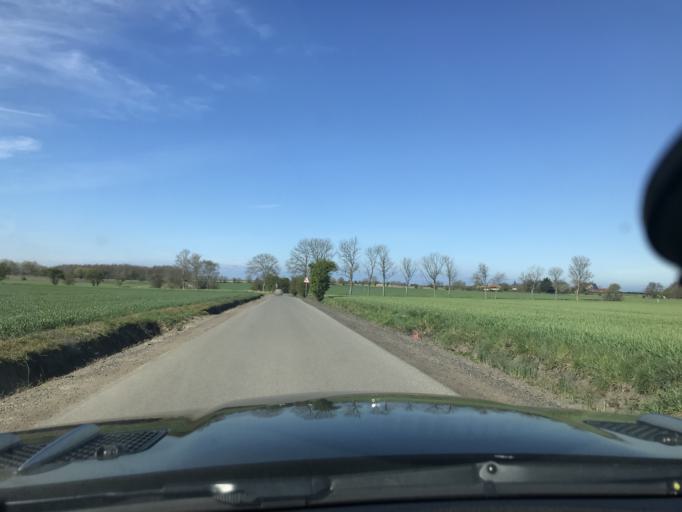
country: DE
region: Schleswig-Holstein
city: Grossenbrode
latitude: 54.4379
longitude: 11.1147
